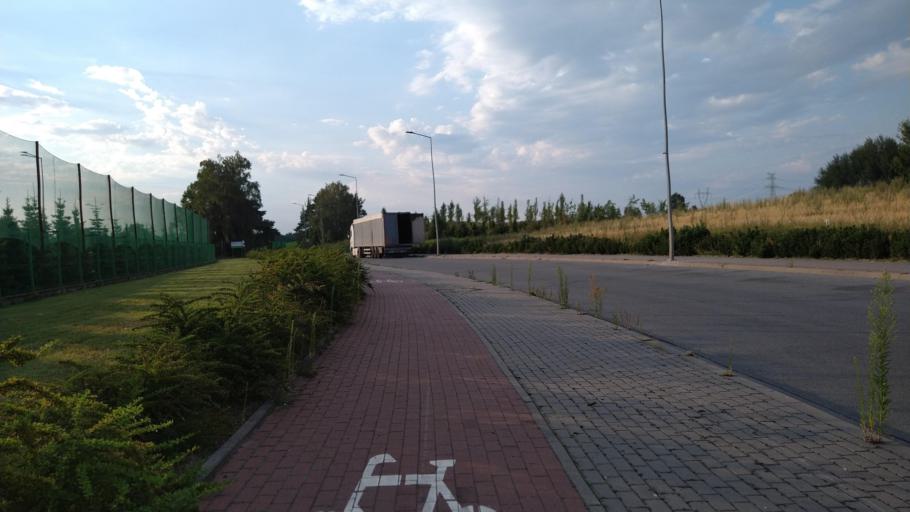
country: PL
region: Warmian-Masurian Voivodeship
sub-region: Powiat olsztynski
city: Olsztyn
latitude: 53.7880
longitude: 20.5538
